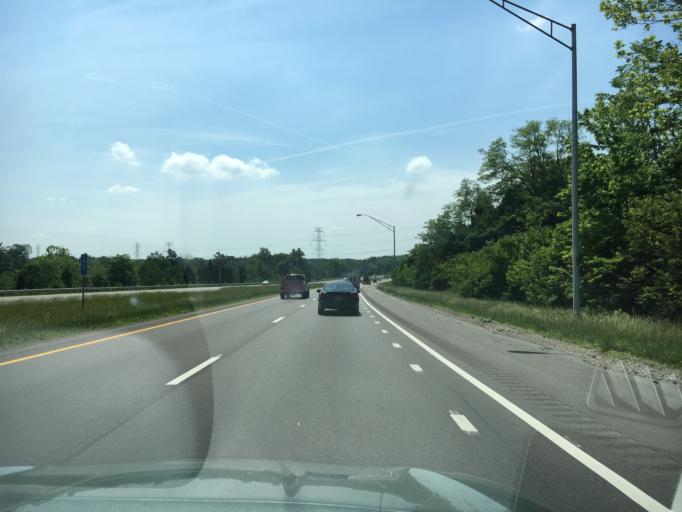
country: US
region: Ohio
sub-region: Hamilton County
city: Monfort Heights
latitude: 39.1822
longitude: -84.5965
